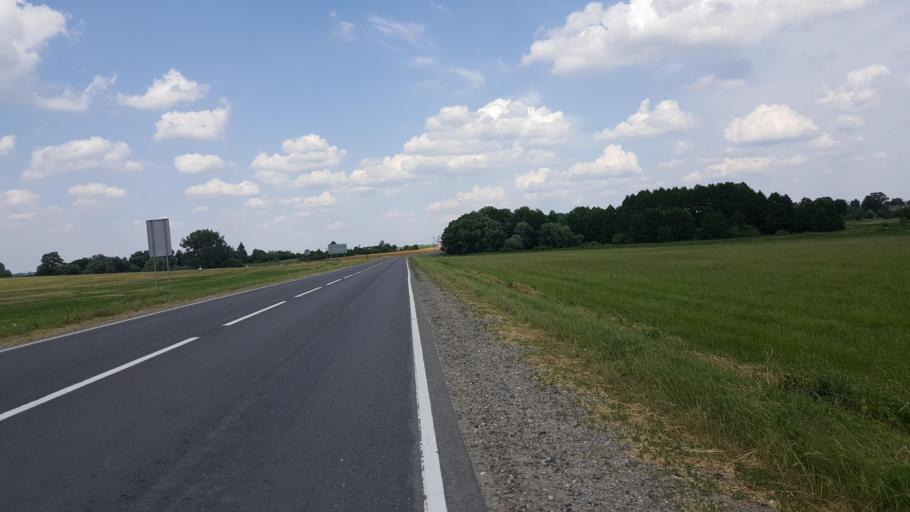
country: BY
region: Brest
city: Kamyanyets
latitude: 52.4014
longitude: 23.7844
